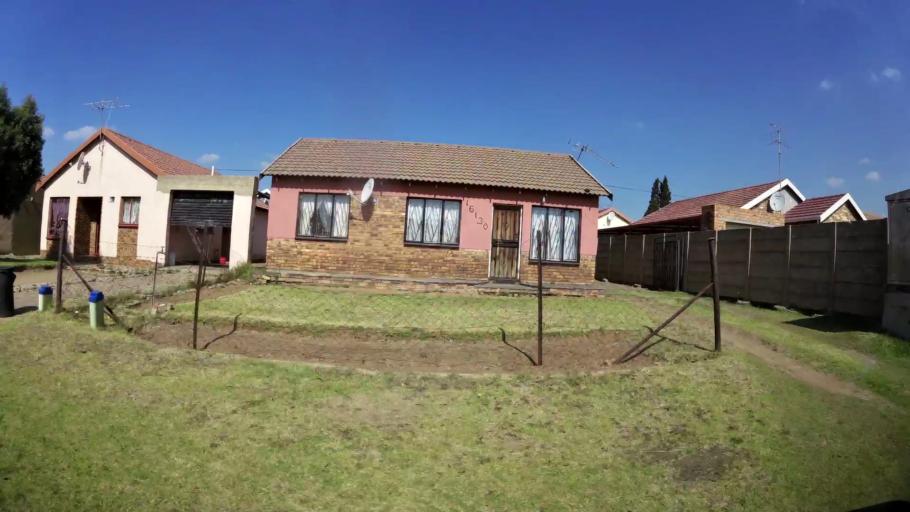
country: ZA
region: Gauteng
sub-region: Ekurhuleni Metropolitan Municipality
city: Benoni
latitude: -26.1456
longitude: 28.4005
